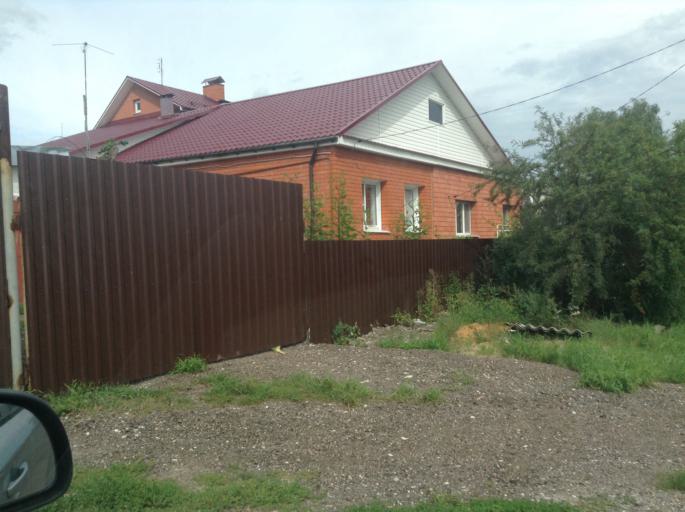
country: RU
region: Moskovskaya
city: Yegor'yevsk
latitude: 55.3623
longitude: 39.0965
